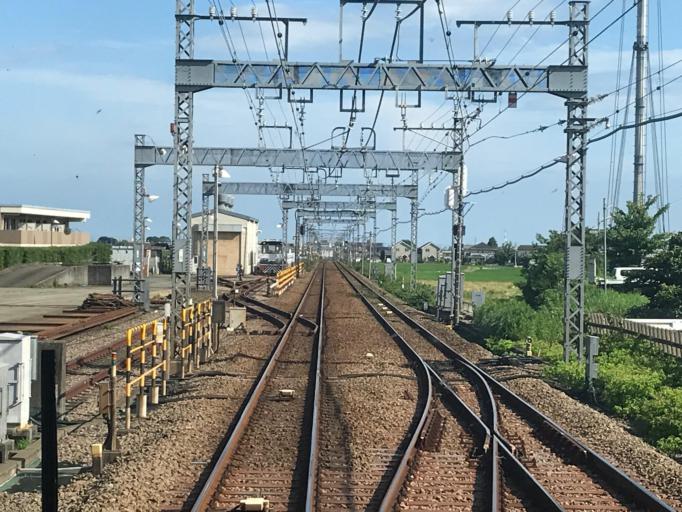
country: JP
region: Kanagawa
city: Odawara
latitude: 35.3245
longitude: 139.1368
